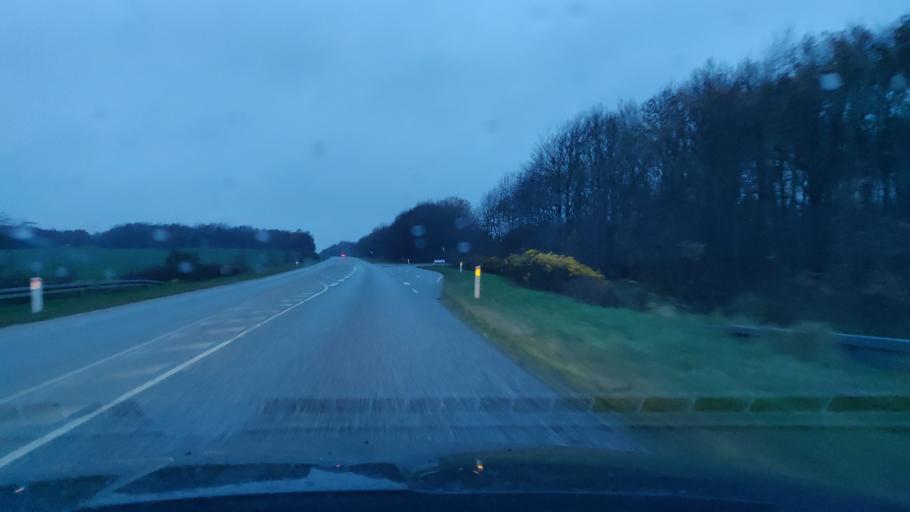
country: DK
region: Central Jutland
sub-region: Herning Kommune
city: Avlum
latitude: 56.2818
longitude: 8.7504
